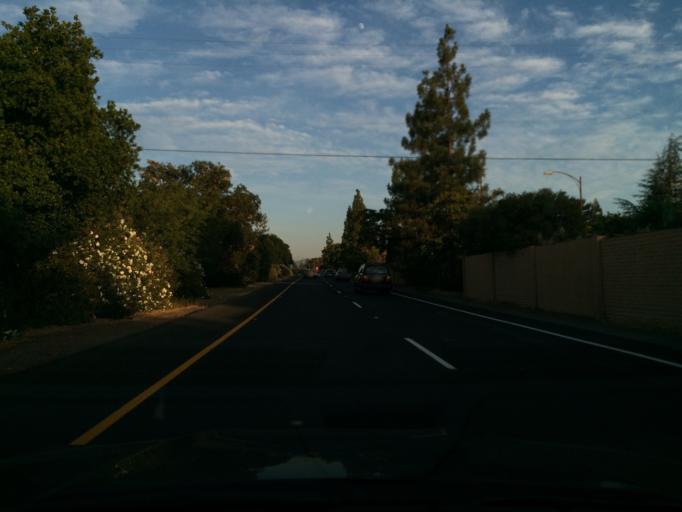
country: US
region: California
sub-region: Santa Clara County
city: Seven Trees
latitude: 37.2242
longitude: -121.8658
